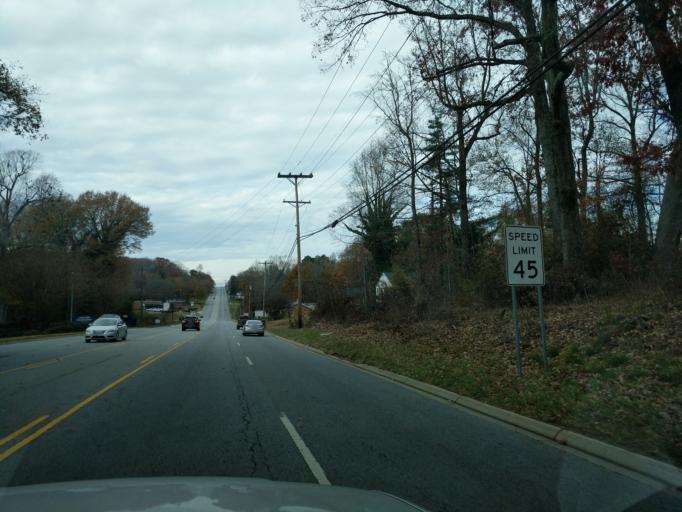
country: US
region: South Carolina
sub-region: Pickens County
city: Arial
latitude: 34.8364
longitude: -82.6259
